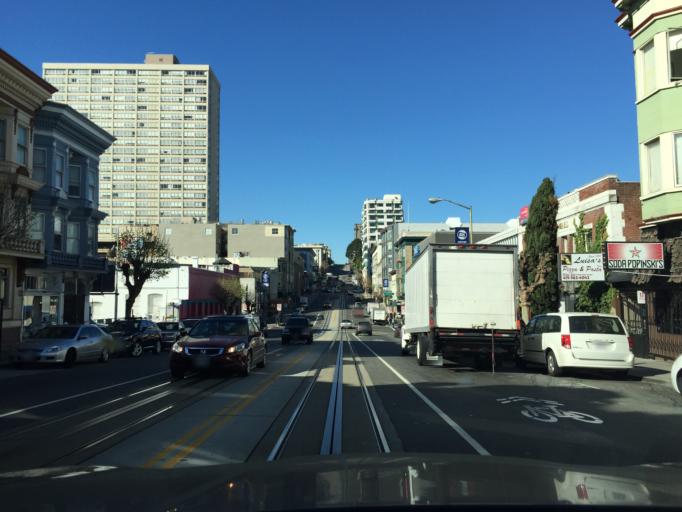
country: US
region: California
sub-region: San Francisco County
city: San Francisco
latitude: 37.7907
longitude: -122.4197
